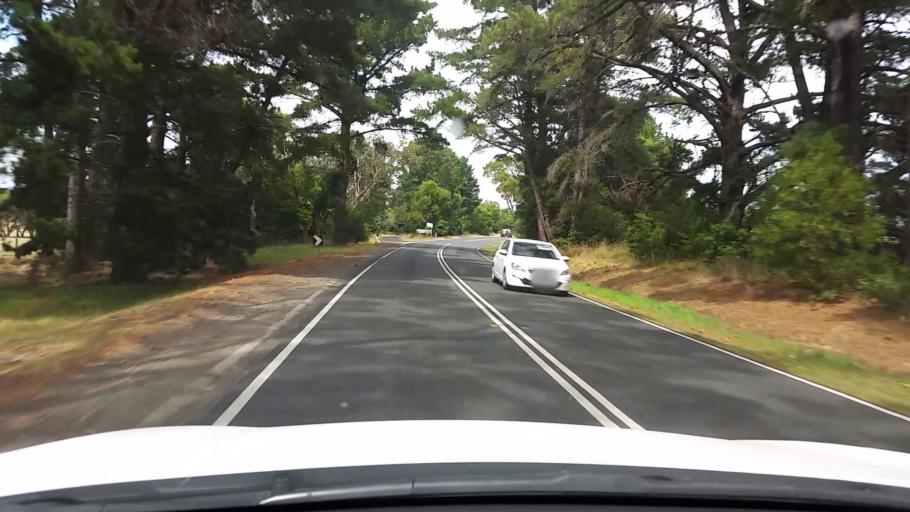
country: AU
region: Victoria
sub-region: Mornington Peninsula
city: Merricks
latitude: -38.3810
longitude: 145.1100
